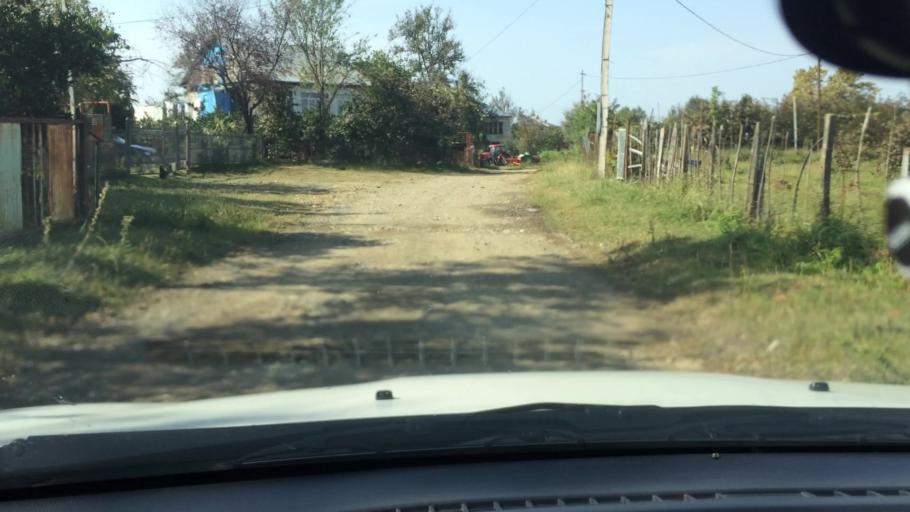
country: GE
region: Ajaria
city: Kobuleti
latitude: 41.8095
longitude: 41.8192
